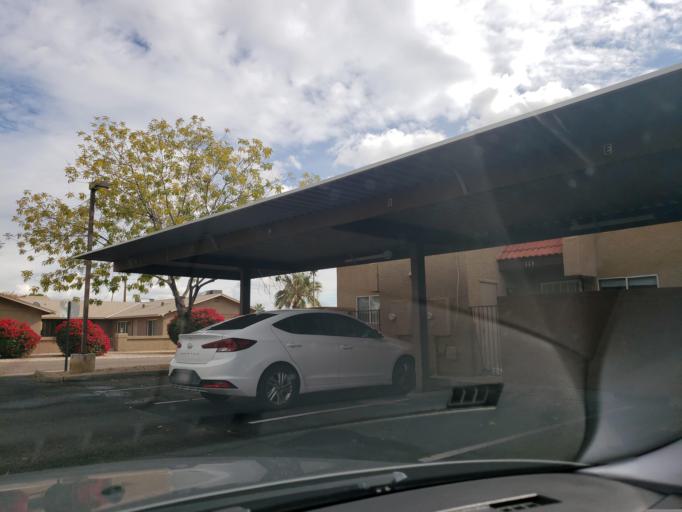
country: US
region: Arizona
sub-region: Maricopa County
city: Paradise Valley
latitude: 33.6520
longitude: -111.9955
